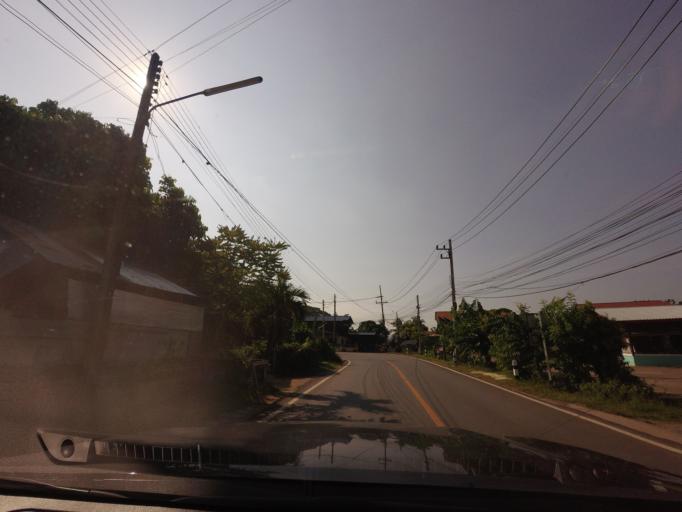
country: TH
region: Nan
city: Nan
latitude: 18.8583
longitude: 100.8170
